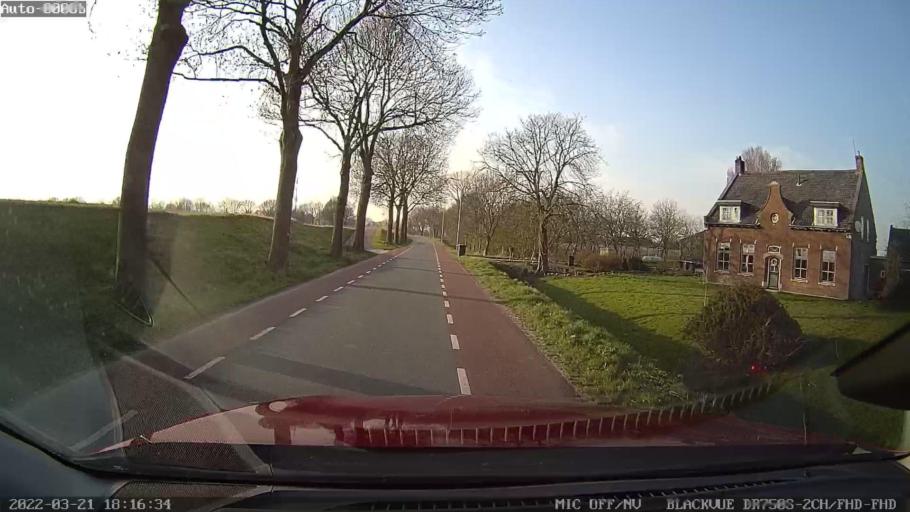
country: NL
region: North Brabant
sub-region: Gemeente Steenbergen
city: Nieuw-Vossemeer
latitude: 51.5801
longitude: 4.2243
